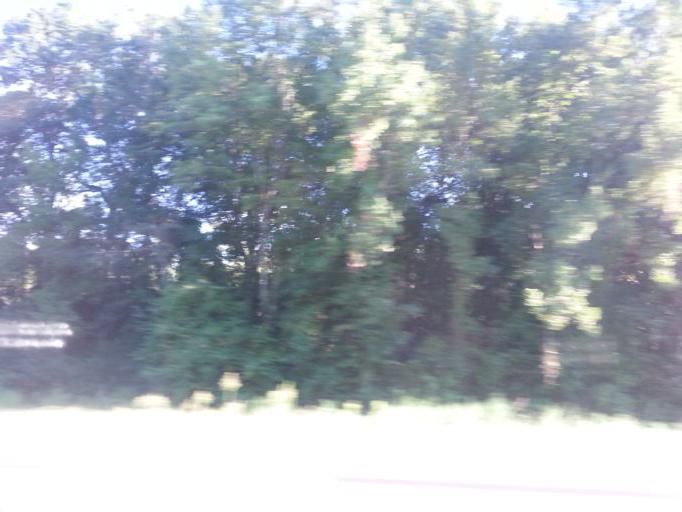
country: US
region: Alabama
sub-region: Lauderdale County
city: Killen
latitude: 34.8597
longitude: -87.5169
